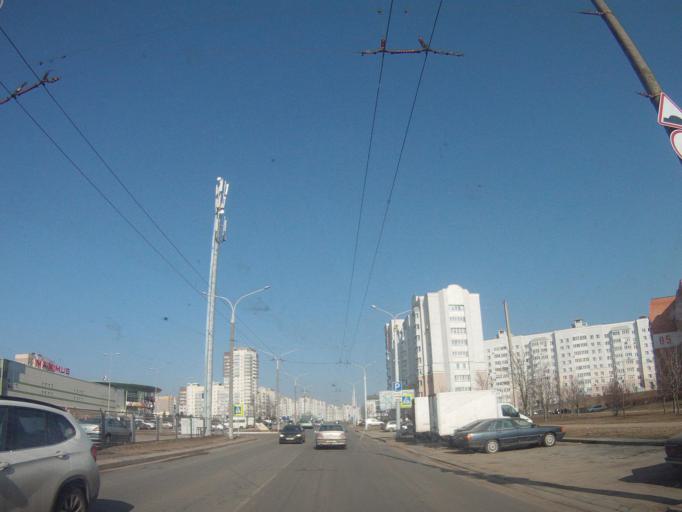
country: BY
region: Minsk
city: Novoye Medvezhino
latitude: 53.8857
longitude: 27.4299
